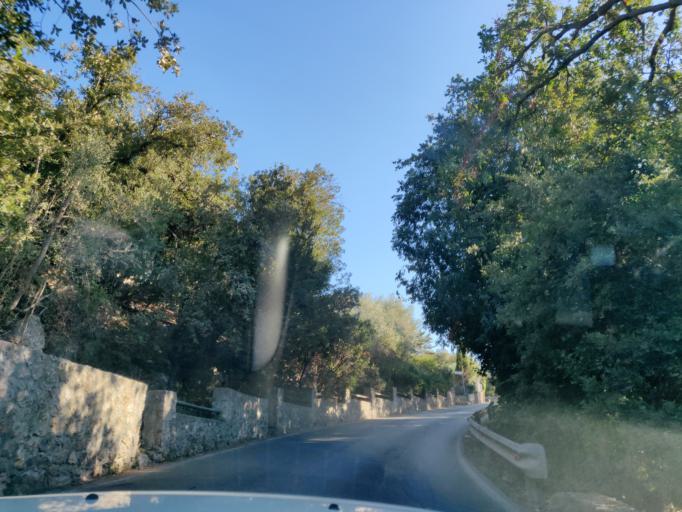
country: IT
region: Tuscany
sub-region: Provincia di Grosseto
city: Orbetello Scalo
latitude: 42.4184
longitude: 11.2825
